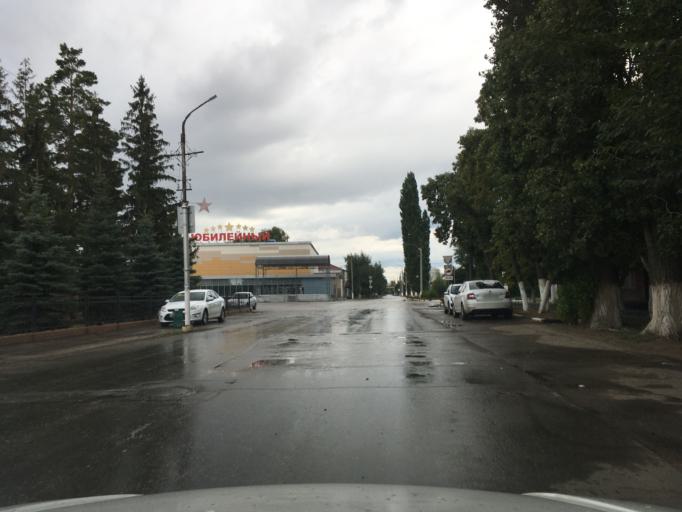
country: RU
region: Samara
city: Bezenchuk
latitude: 52.9843
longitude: 49.4398
